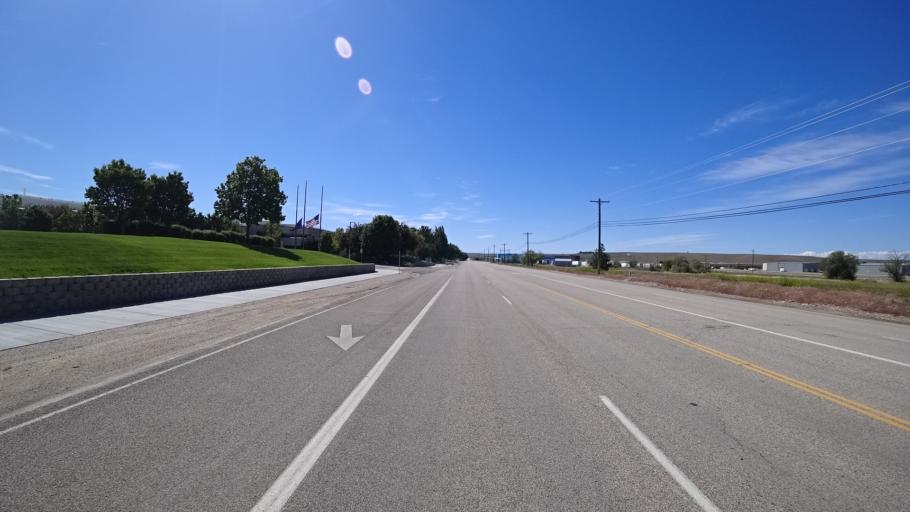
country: US
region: Idaho
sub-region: Ada County
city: Boise
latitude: 43.5296
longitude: -116.1506
